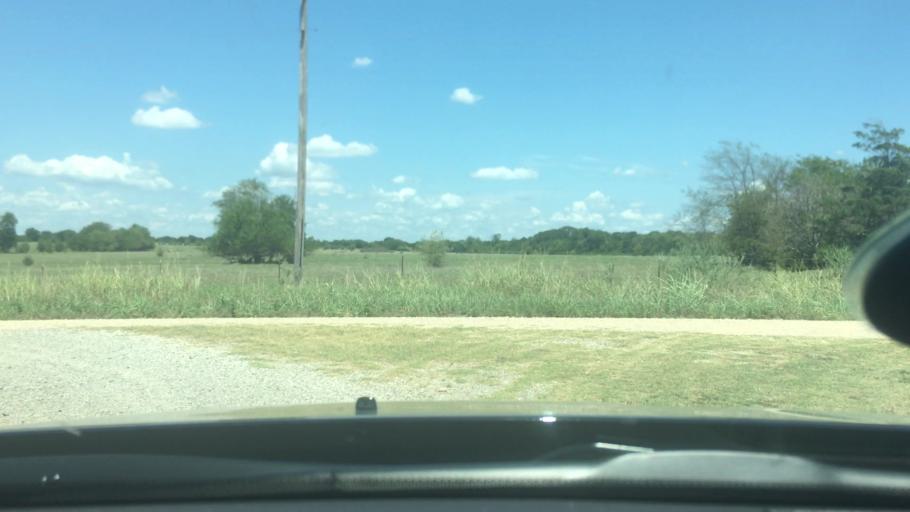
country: US
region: Oklahoma
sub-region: Bryan County
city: Durant
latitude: 33.9971
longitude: -96.0969
